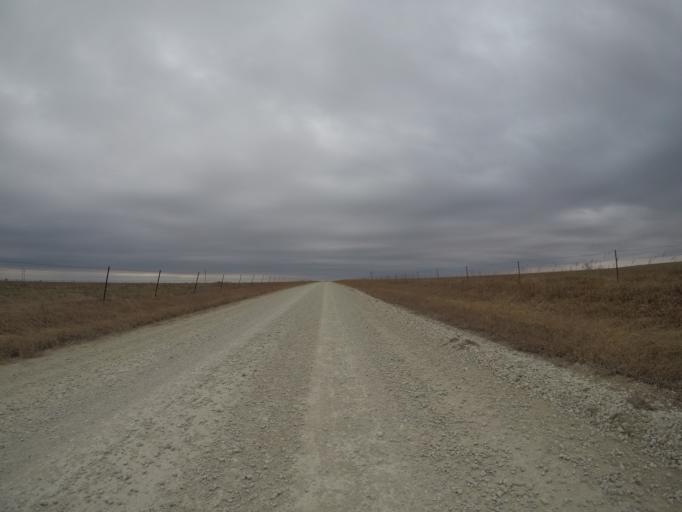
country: US
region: Kansas
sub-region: Wabaunsee County
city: Alma
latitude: 38.7582
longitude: -96.1496
